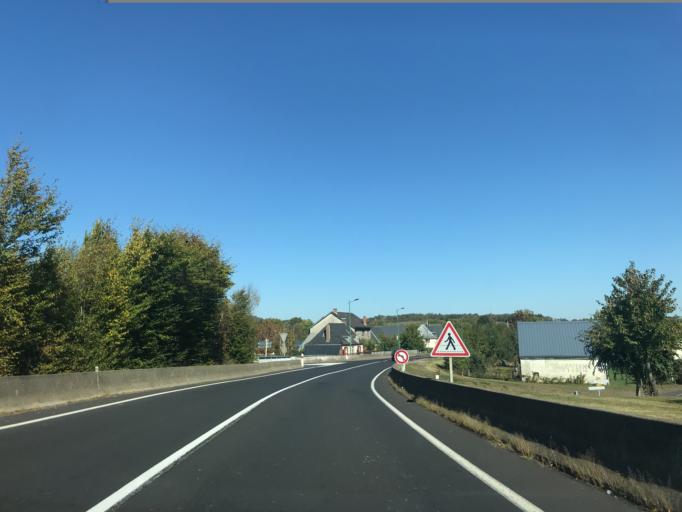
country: FR
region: Auvergne
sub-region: Departement du Puy-de-Dome
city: Gelles
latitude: 45.7229
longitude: 2.8013
